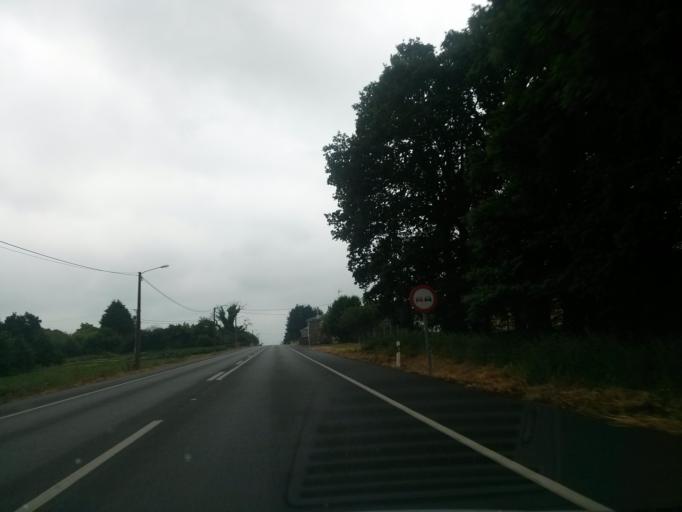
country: ES
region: Galicia
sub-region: Provincia de Lugo
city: Begonte
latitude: 43.1344
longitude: -7.6569
